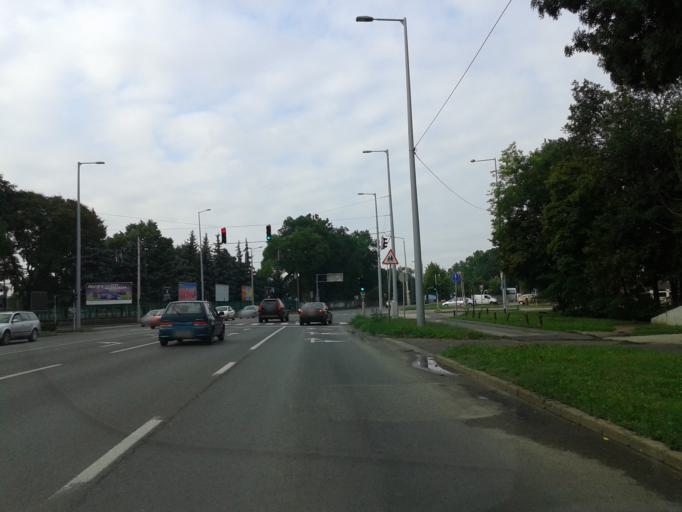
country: HU
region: Csongrad
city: Szeged
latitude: 46.2455
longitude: 20.1643
